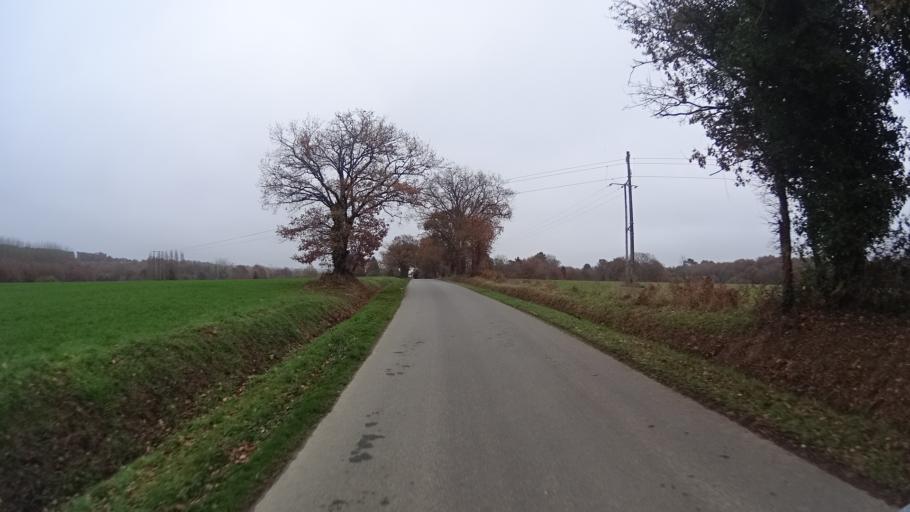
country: FR
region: Brittany
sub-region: Departement d'Ille-et-Vilaine
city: Sainte-Marie
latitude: 47.7095
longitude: -2.0055
